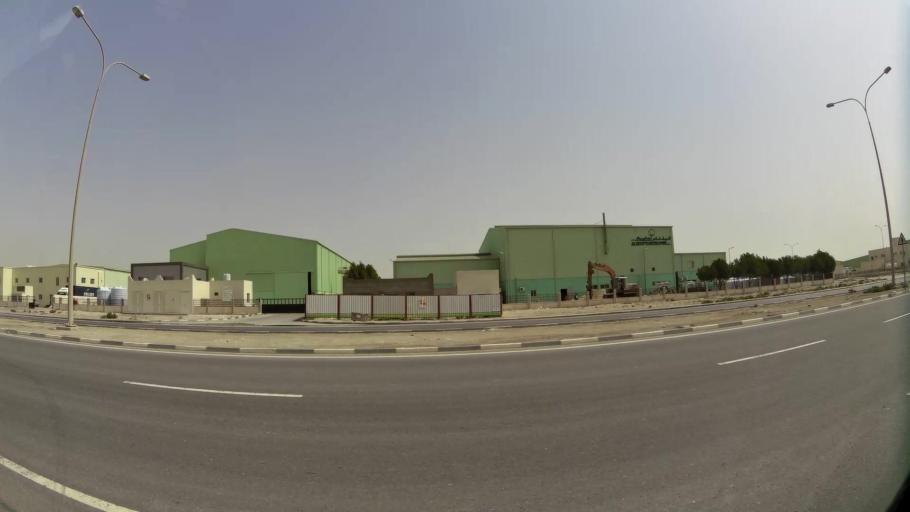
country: QA
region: Al Wakrah
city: Al Wukayr
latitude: 25.1573
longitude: 51.4100
